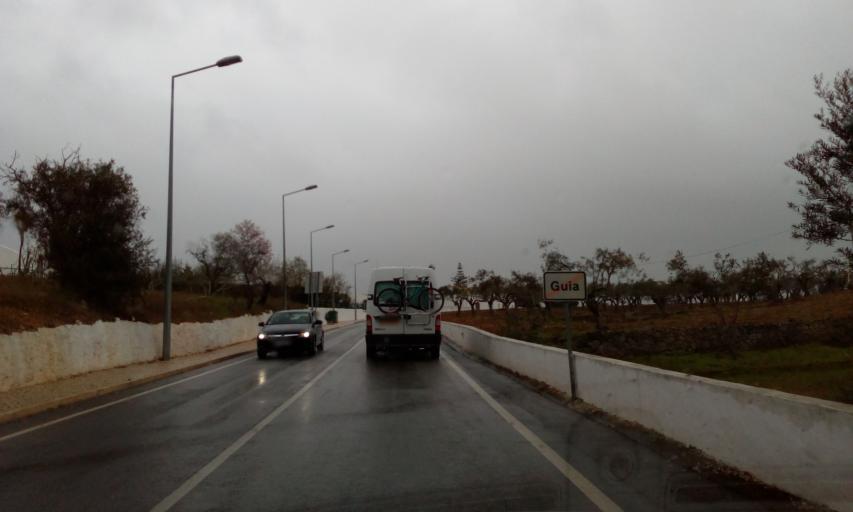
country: PT
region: Faro
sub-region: Albufeira
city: Guia
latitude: 37.1245
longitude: -8.2966
